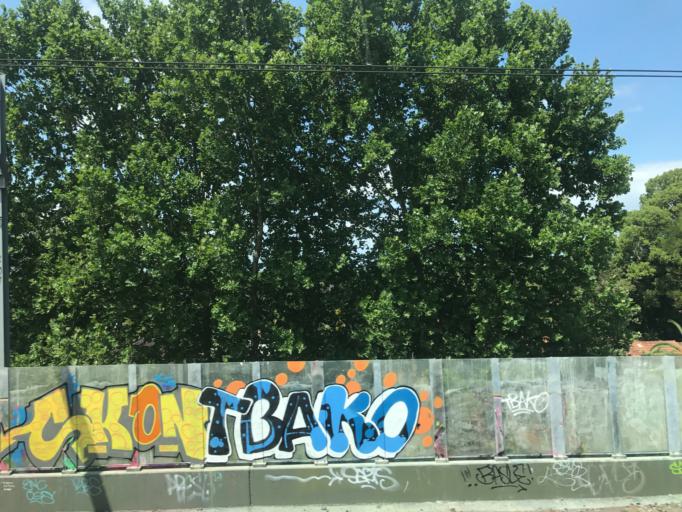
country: AU
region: New South Wales
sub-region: Willoughby
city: Chatswood
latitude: -33.7879
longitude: 151.1804
